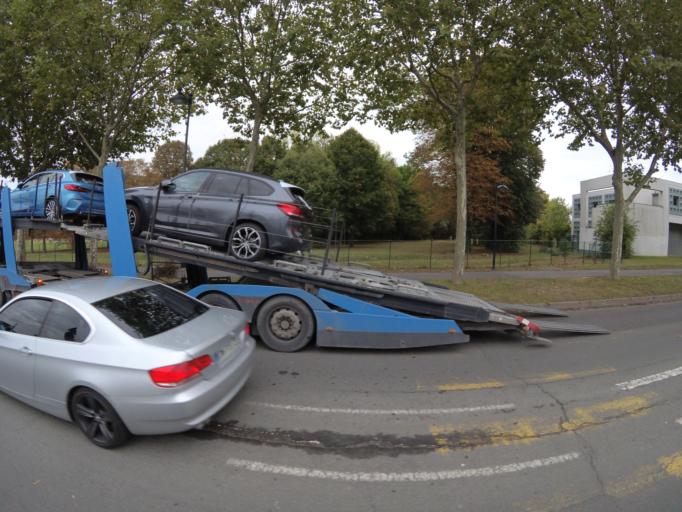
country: FR
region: Ile-de-France
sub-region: Departement de Seine-et-Marne
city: Saint-Thibault-des-Vignes
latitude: 48.8594
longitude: 2.6714
